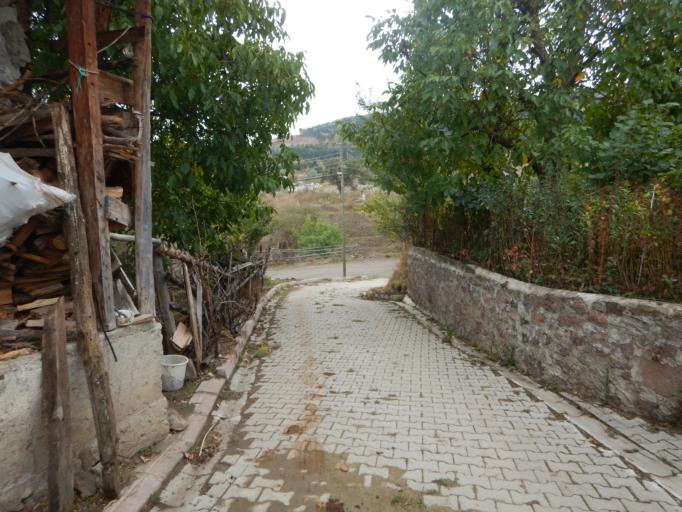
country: TR
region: Ordu
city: Mesudiye
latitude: 40.4334
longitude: 37.7789
